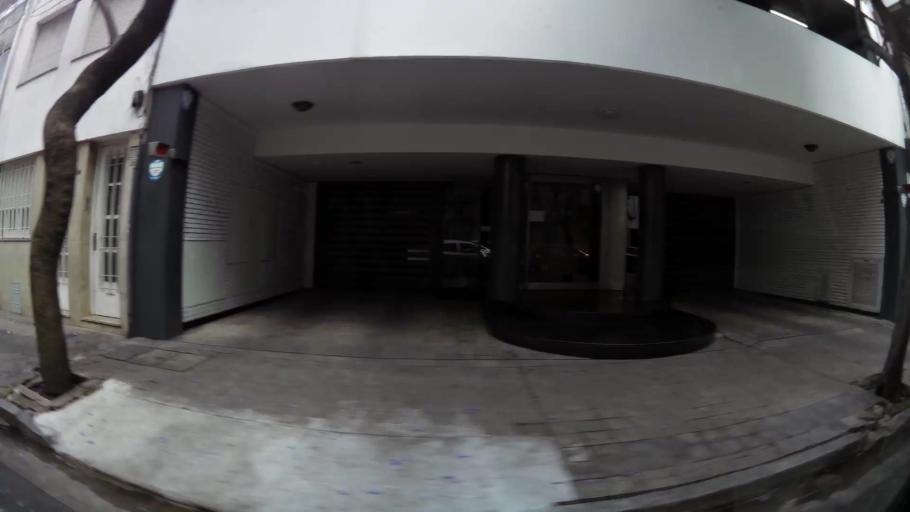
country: AR
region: Santa Fe
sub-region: Departamento de Rosario
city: Rosario
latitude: -32.9392
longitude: -60.6384
